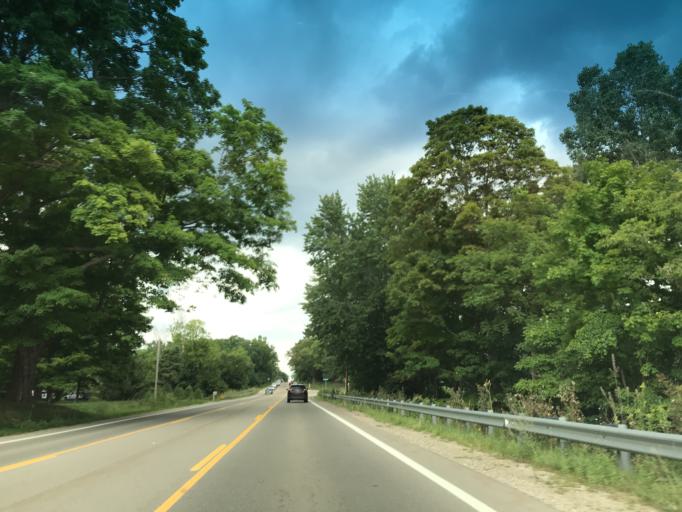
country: US
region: Michigan
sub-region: Oakland County
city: Milford
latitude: 42.5409
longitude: -83.6172
